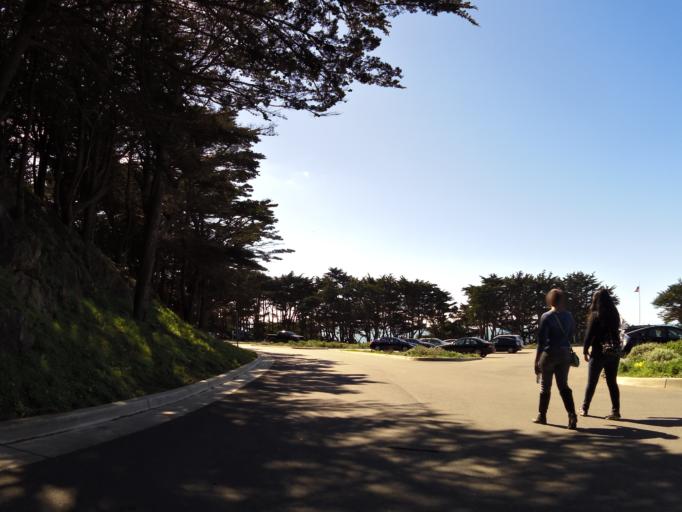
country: US
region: California
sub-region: Marin County
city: Sausalito
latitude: 37.7831
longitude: -122.5106
